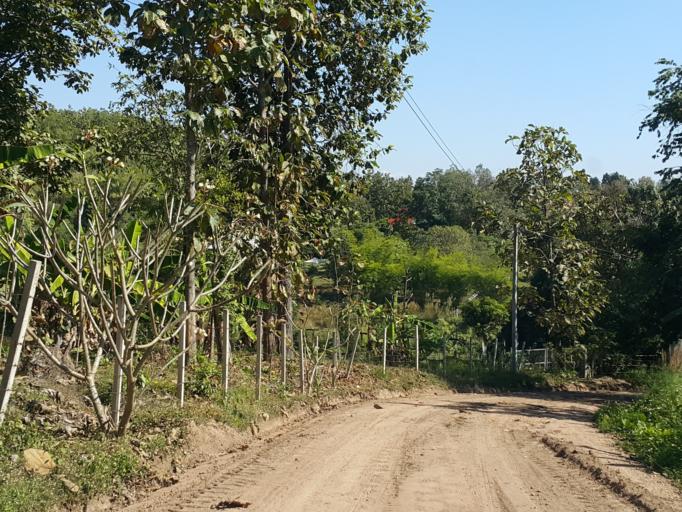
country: TH
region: Chiang Mai
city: Mae Taeng
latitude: 18.9537
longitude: 98.9029
